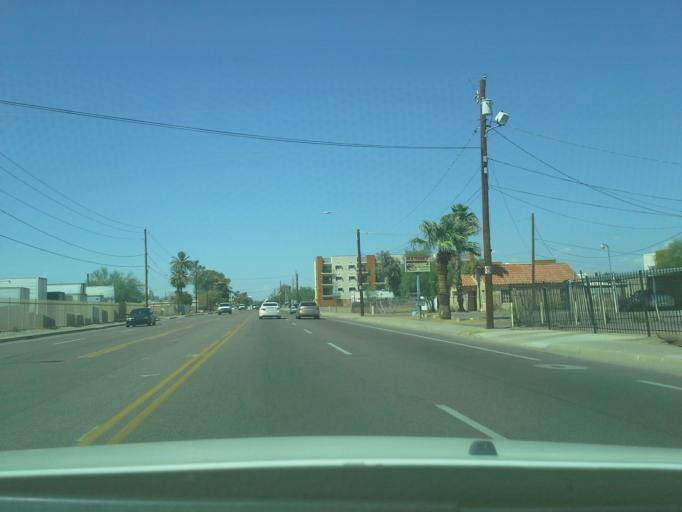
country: US
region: Arizona
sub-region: Maricopa County
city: Phoenix
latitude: 33.4076
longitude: -112.0645
